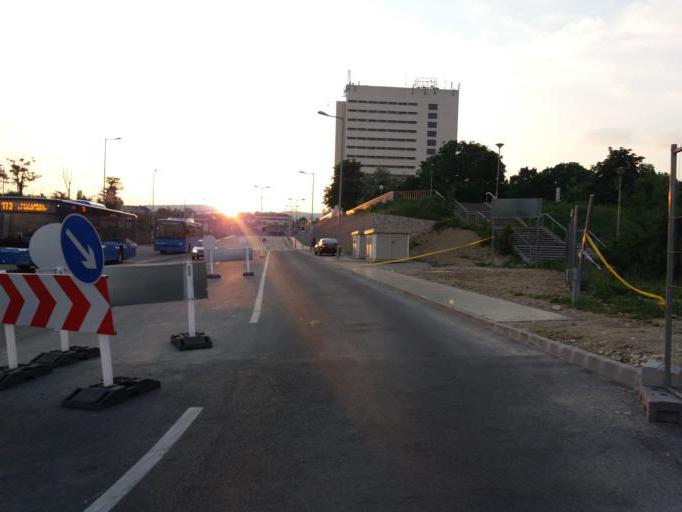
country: HU
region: Budapest
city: Budapest XI. keruelet
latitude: 47.4647
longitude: 19.0188
